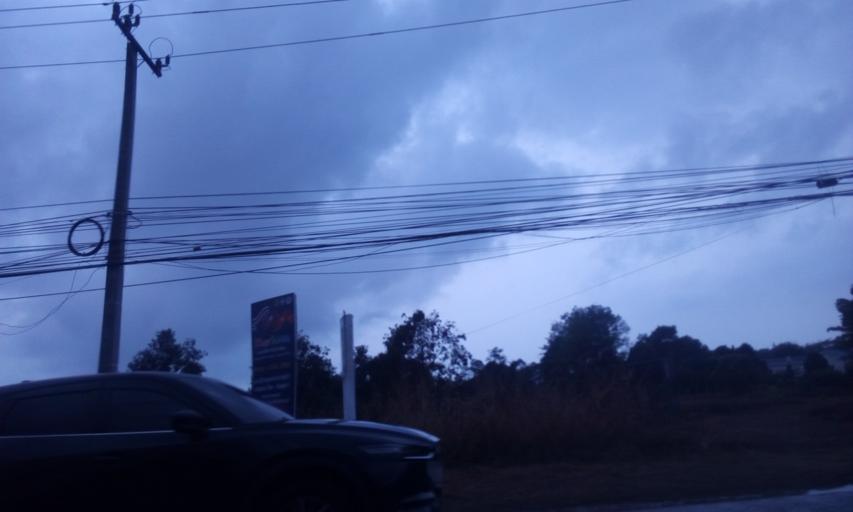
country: TH
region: Chanthaburi
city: Khlung
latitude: 12.4595
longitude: 102.2310
